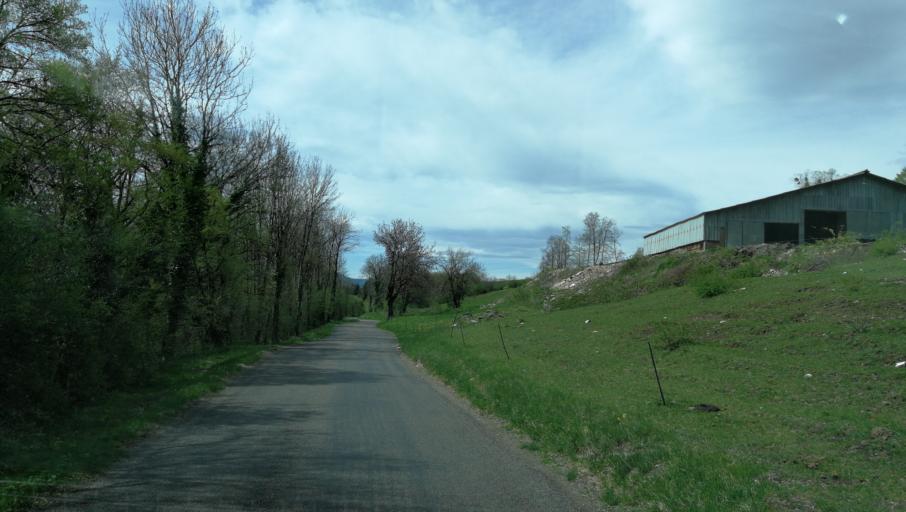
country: FR
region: Rhone-Alpes
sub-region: Departement de l'Ain
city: Arbent
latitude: 46.2443
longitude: 5.7702
